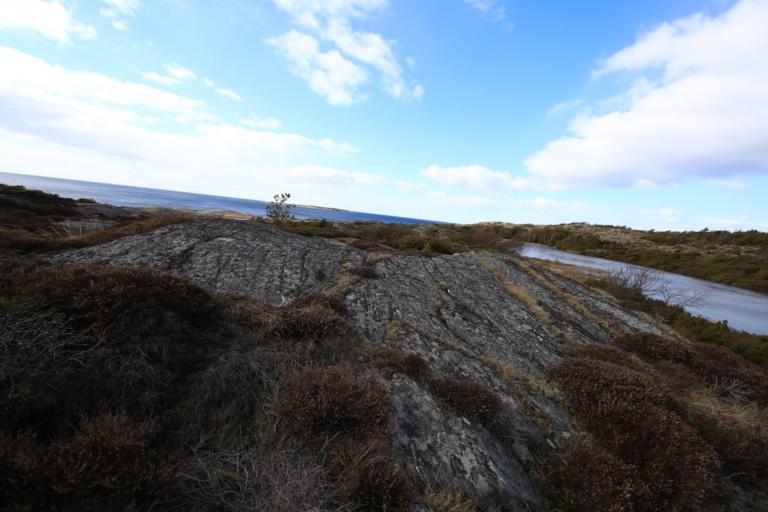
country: SE
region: Halland
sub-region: Kungsbacka Kommun
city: Frillesas
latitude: 57.2198
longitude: 12.1346
